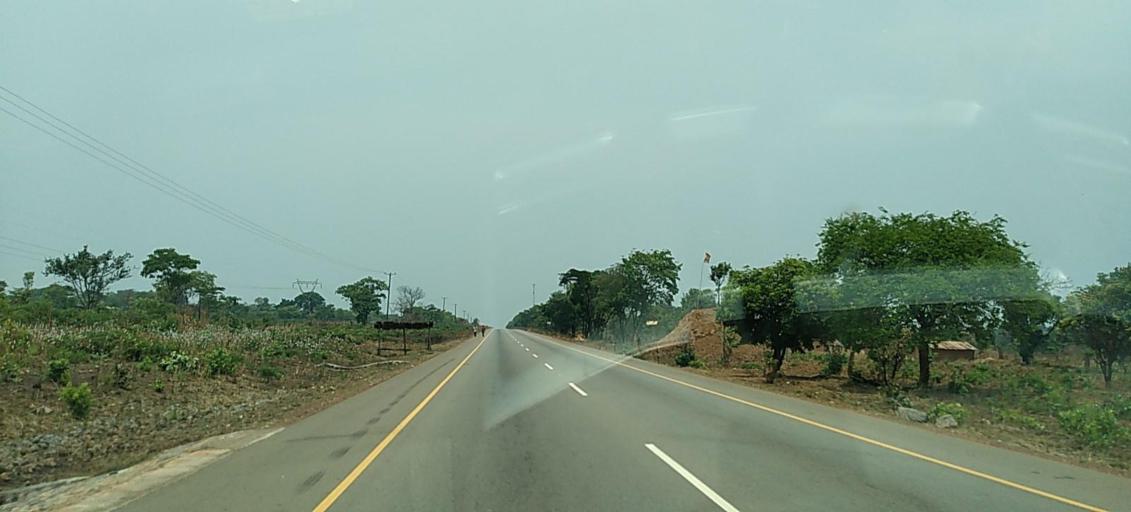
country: ZM
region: Copperbelt
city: Chililabombwe
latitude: -12.4240
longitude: 27.4024
